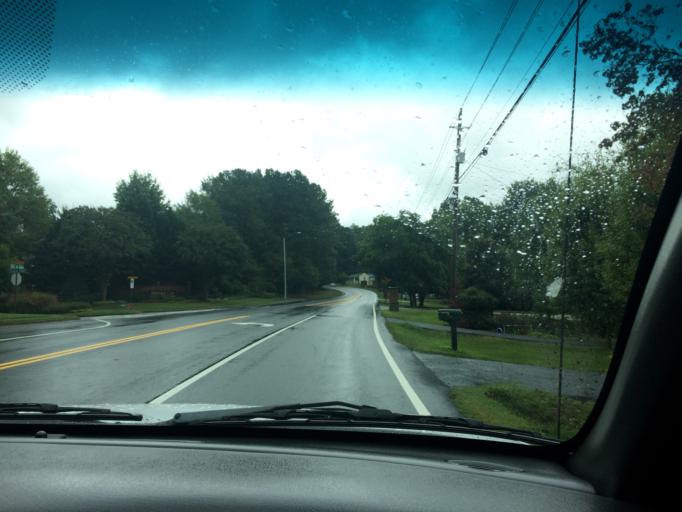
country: US
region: Georgia
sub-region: Cobb County
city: Kennesaw
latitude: 34.0351
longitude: -84.6420
